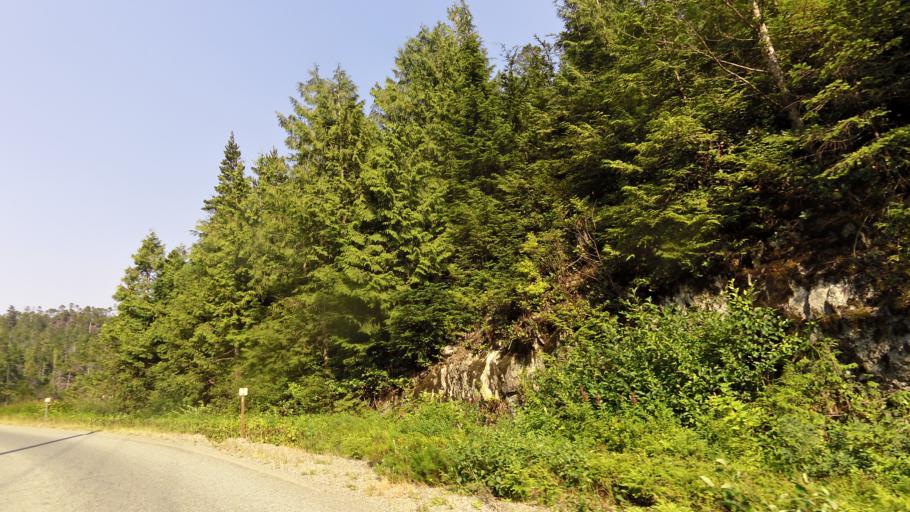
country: CA
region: British Columbia
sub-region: Regional District of Alberni-Clayoquot
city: Ucluelet
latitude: 49.1084
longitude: -125.4545
